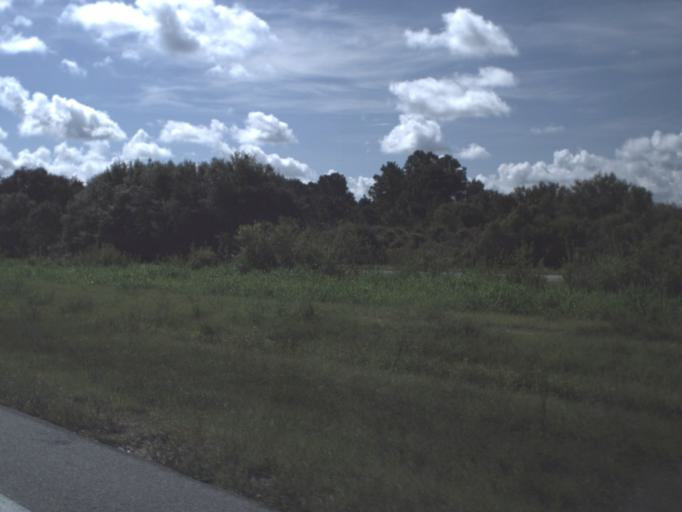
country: US
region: Florida
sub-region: Sarasota County
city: Warm Mineral Springs
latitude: 27.1080
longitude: -82.3070
